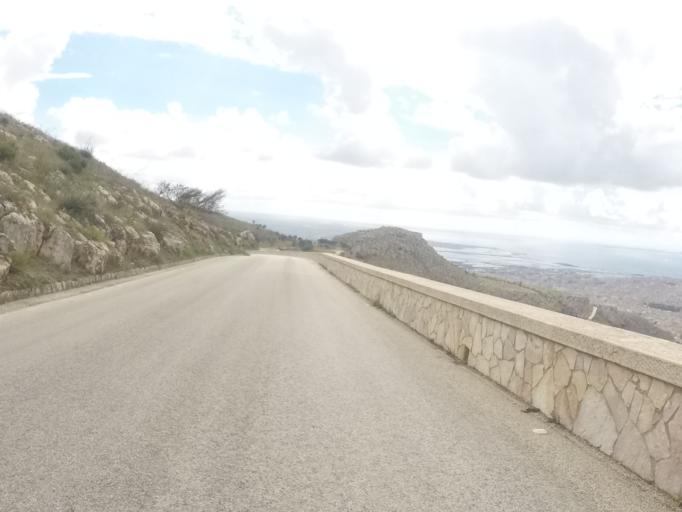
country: IT
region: Sicily
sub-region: Trapani
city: Erice
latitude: 38.0431
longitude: 12.5666
